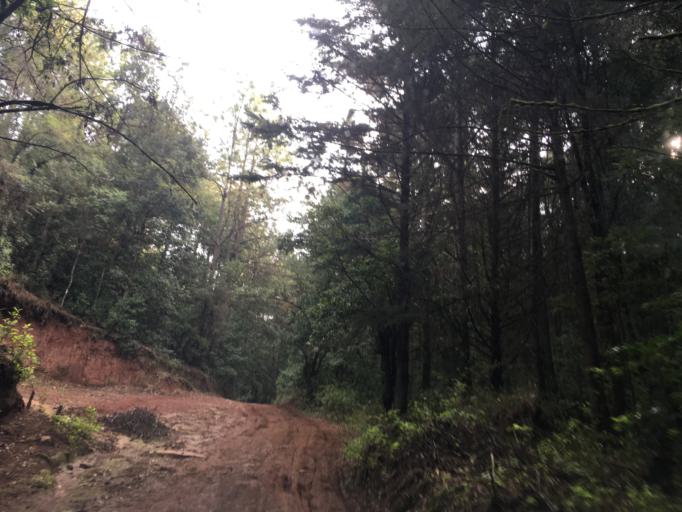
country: MX
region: Michoacan
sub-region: Zitacuaro
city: La Fundicion (Quinta Manzana)
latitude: 19.4953
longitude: -100.3120
